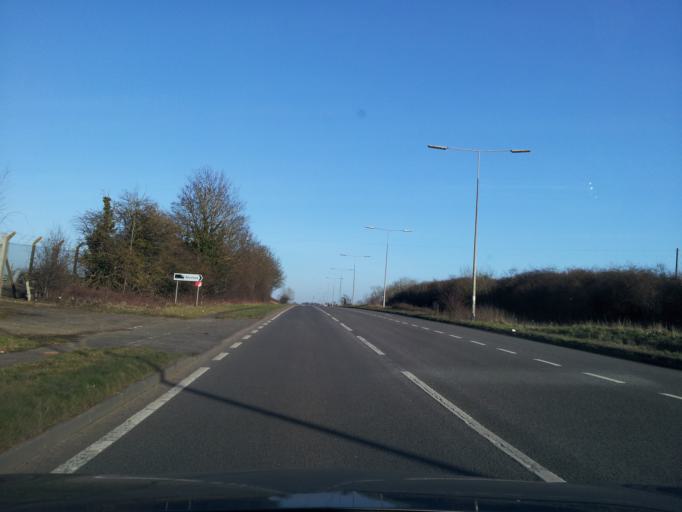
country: GB
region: England
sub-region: Northamptonshire
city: Bugbrooke
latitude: 52.2326
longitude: -1.0037
